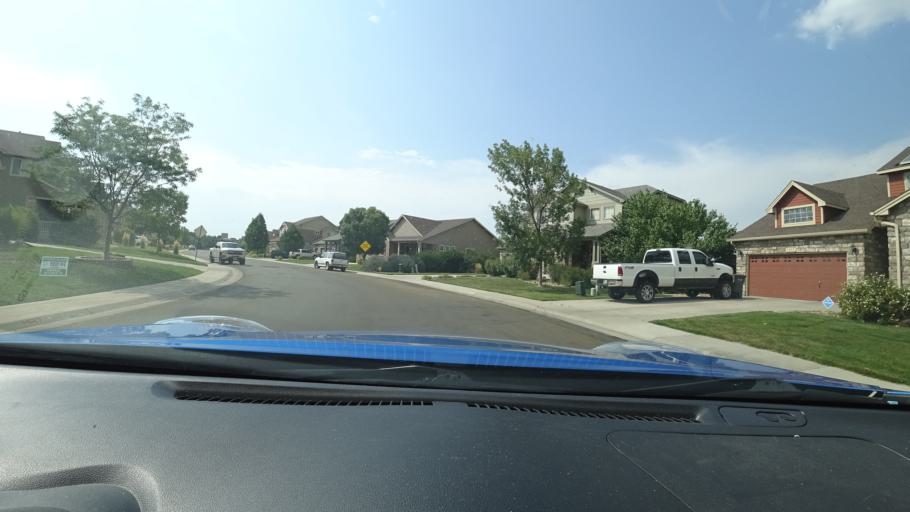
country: US
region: Colorado
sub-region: Adams County
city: Todd Creek
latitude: 39.9332
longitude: -104.9047
